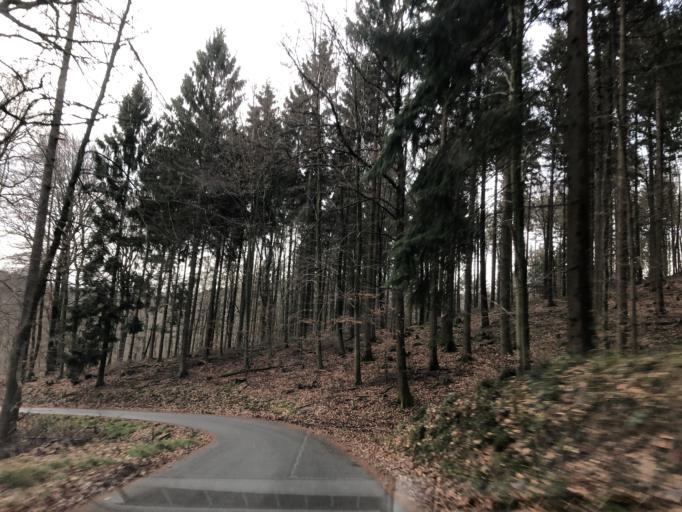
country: DE
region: Baden-Wuerttemberg
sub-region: Karlsruhe Region
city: Dossenheim
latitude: 49.4486
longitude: 8.6907
